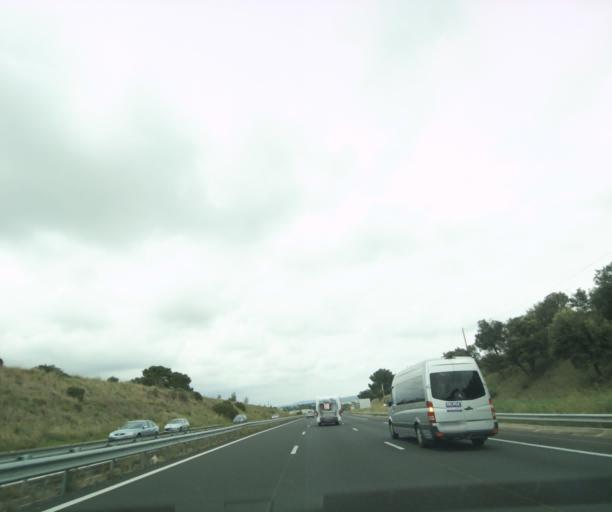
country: FR
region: Languedoc-Roussillon
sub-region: Departement de l'Herault
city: Poussan
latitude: 43.4775
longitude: 3.6555
